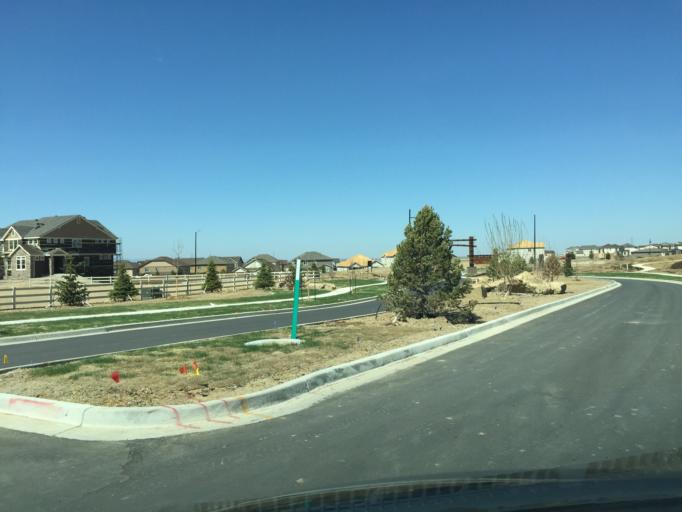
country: US
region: Colorado
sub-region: Boulder County
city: Erie
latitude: 40.0424
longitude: -105.0328
